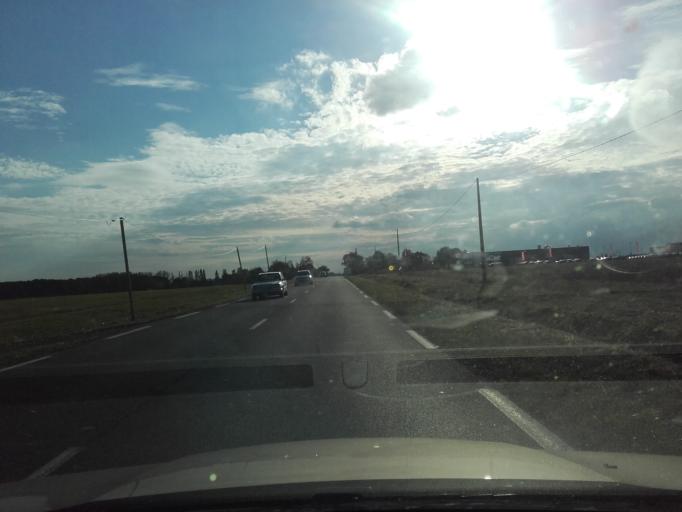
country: FR
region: Centre
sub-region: Departement d'Indre-et-Loire
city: Parcay-Meslay
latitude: 47.4690
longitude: 0.7507
